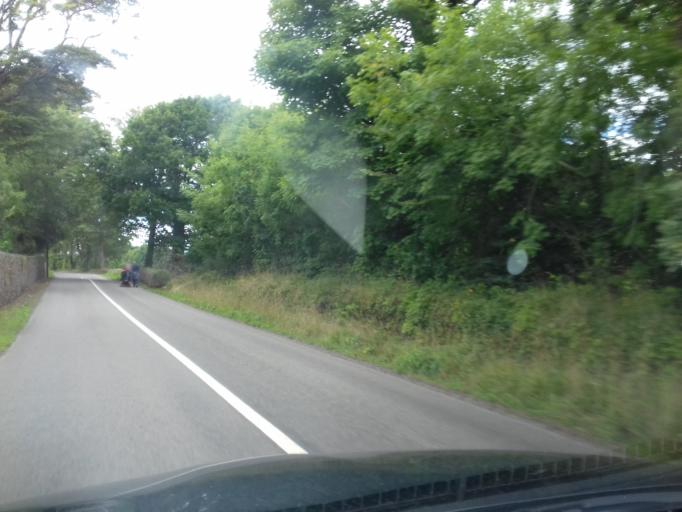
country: IE
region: Munster
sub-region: Waterford
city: Portlaw
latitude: 52.1784
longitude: -7.3413
